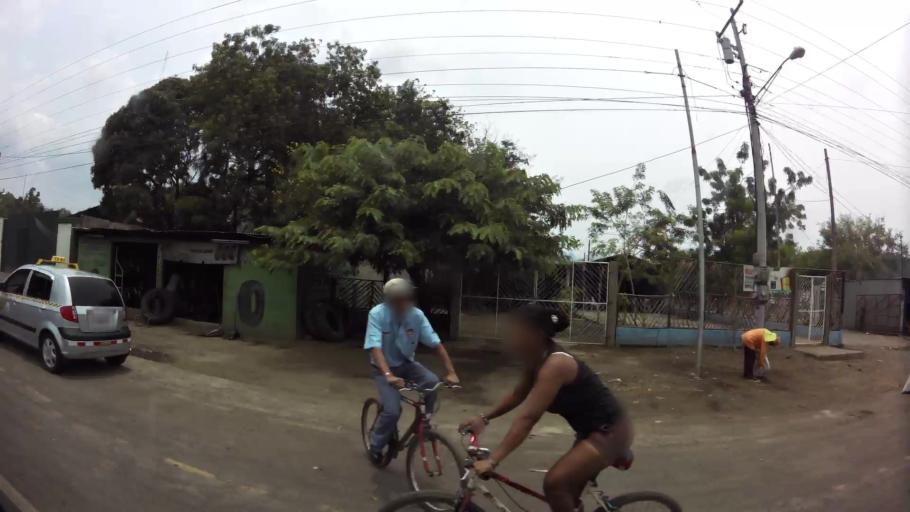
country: NI
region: Leon
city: Leon
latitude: 12.4304
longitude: -86.8645
